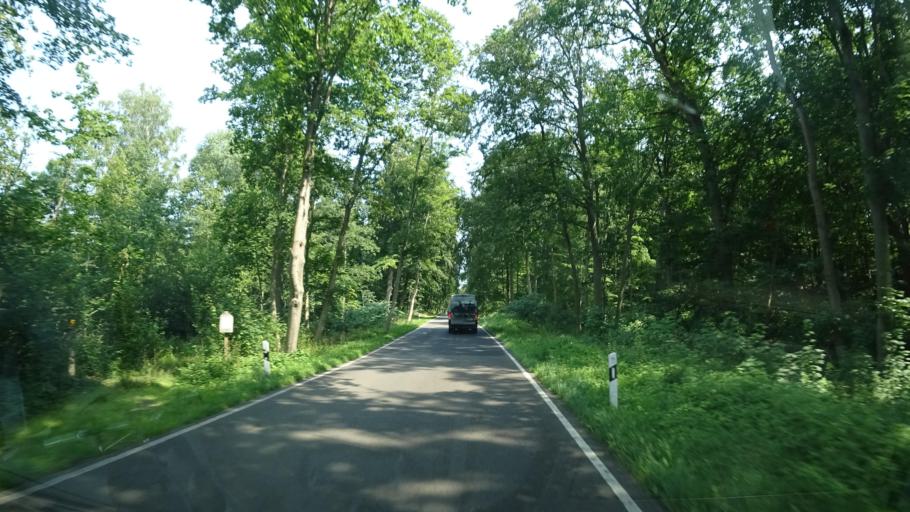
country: PL
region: West Pomeranian Voivodeship
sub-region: Swinoujscie
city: Swinoujscie
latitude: 53.8905
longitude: 14.1957
